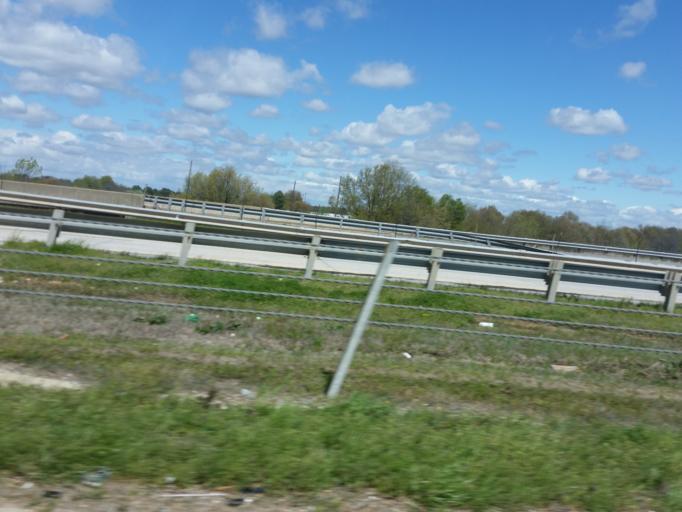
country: US
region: Arkansas
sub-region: Craighead County
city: Jonesboro
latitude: 35.8069
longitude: -90.6575
